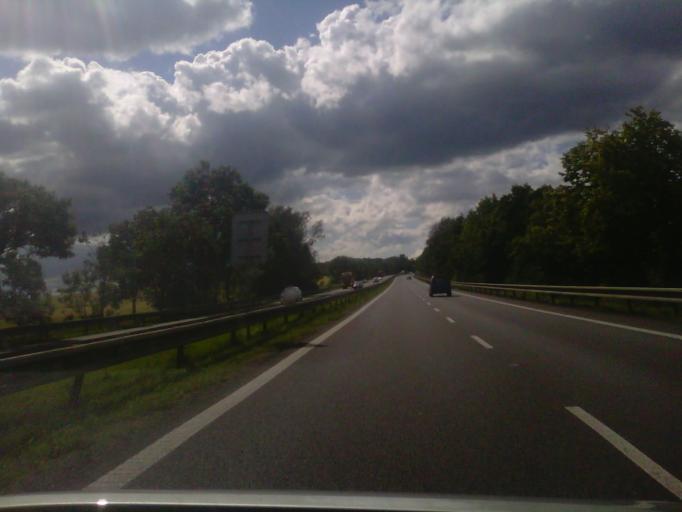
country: CZ
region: Olomoucky
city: Horka nad Moravou
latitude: 49.6080
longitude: 17.2063
